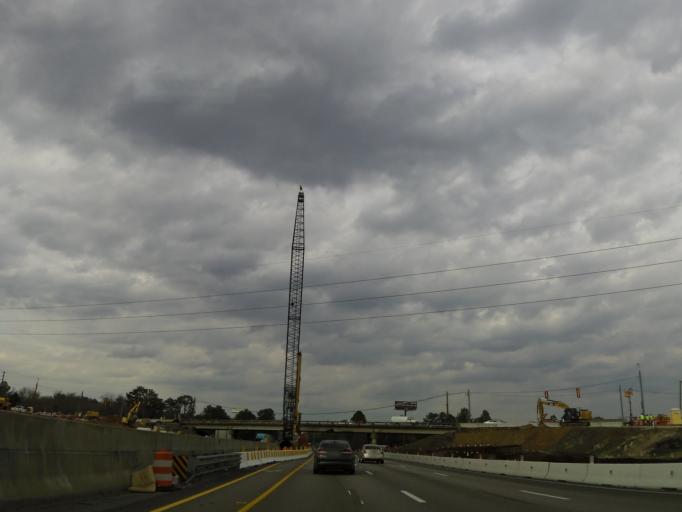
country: US
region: South Carolina
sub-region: Lexington County
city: Springdale
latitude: 33.9878
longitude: -81.1072
